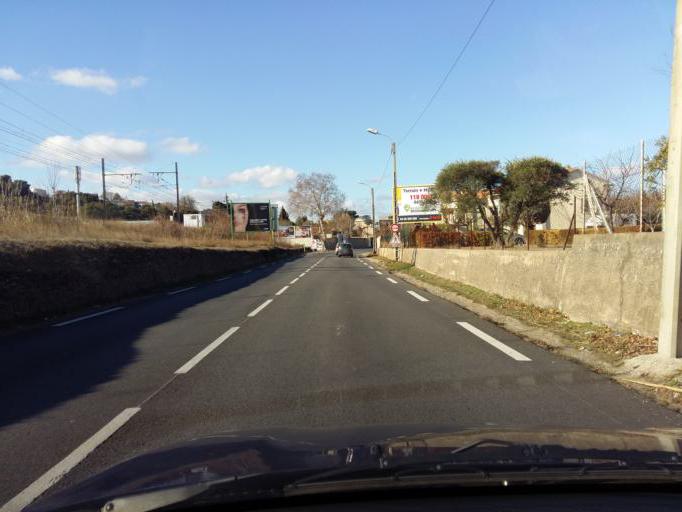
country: FR
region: Languedoc-Roussillon
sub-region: Departement du Gard
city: Bagnols-sur-Ceze
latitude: 44.1560
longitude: 4.6379
